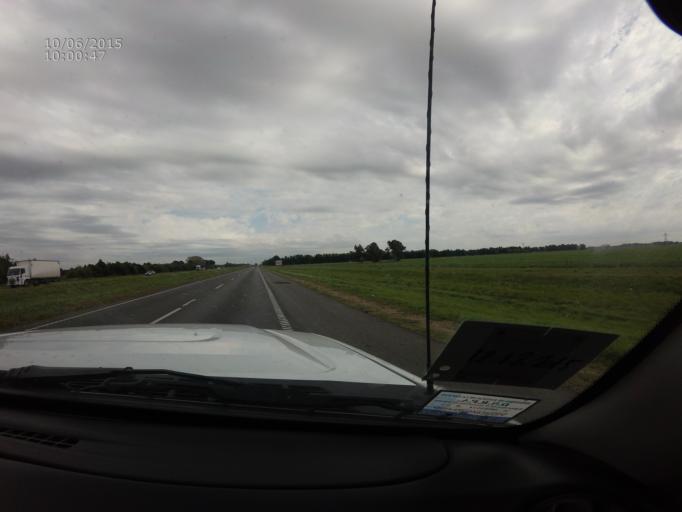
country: AR
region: Buenos Aires
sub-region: Partido de Baradero
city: Baradero
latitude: -33.8907
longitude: -59.4848
